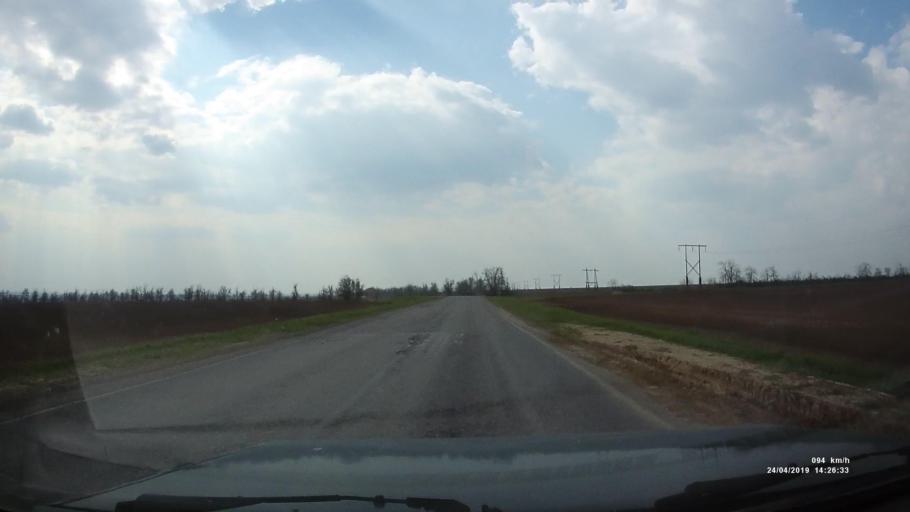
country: RU
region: Kalmykiya
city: Arshan'
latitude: 46.3341
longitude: 44.0602
